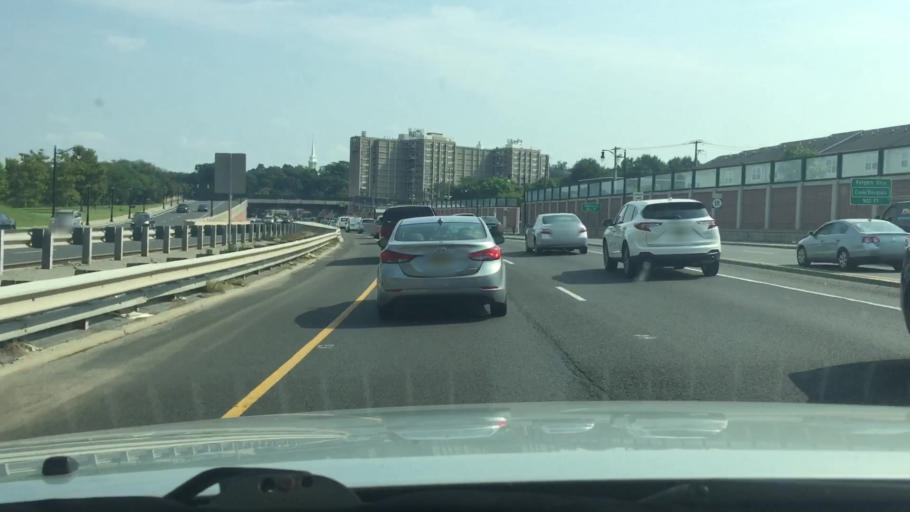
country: US
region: New Jersey
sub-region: Middlesex County
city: New Brunswick
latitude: 40.4920
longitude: -74.4385
